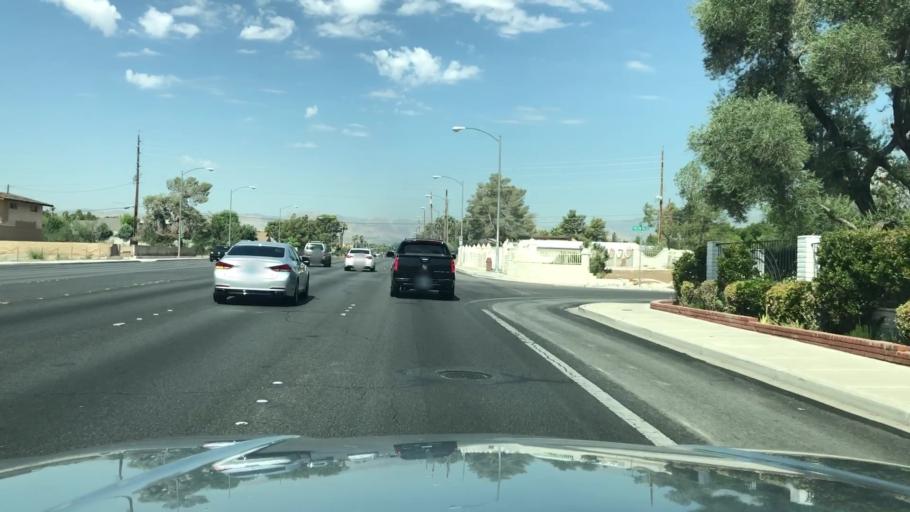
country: US
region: Nevada
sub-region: Clark County
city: Spring Valley
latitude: 36.1296
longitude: -115.2183
